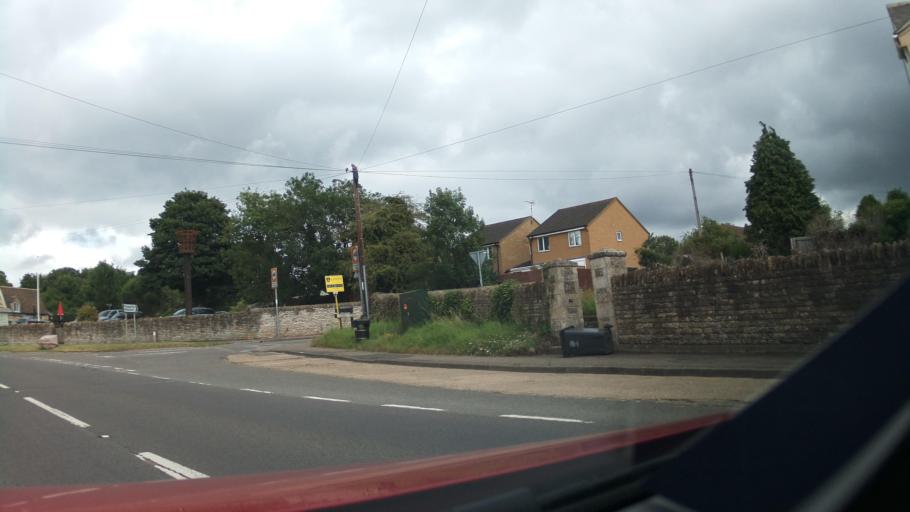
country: GB
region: England
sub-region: District of Rutland
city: Ketton
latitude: 52.6131
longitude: -0.5302
